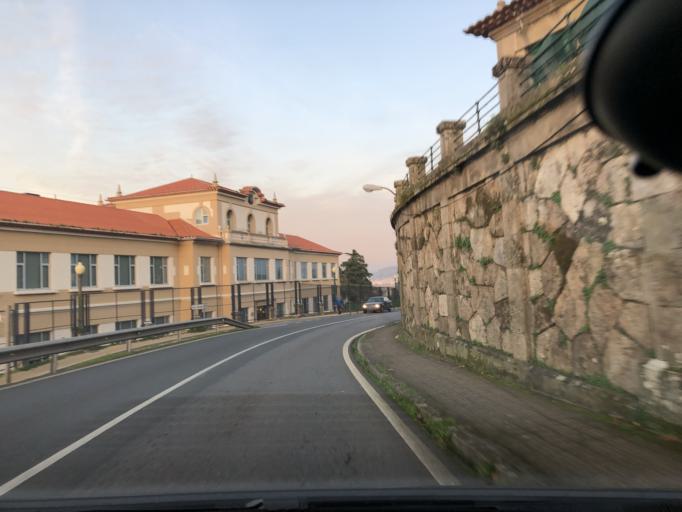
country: ES
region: Galicia
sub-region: Provincia de Pontevedra
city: Marin
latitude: 42.3936
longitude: -8.7096
